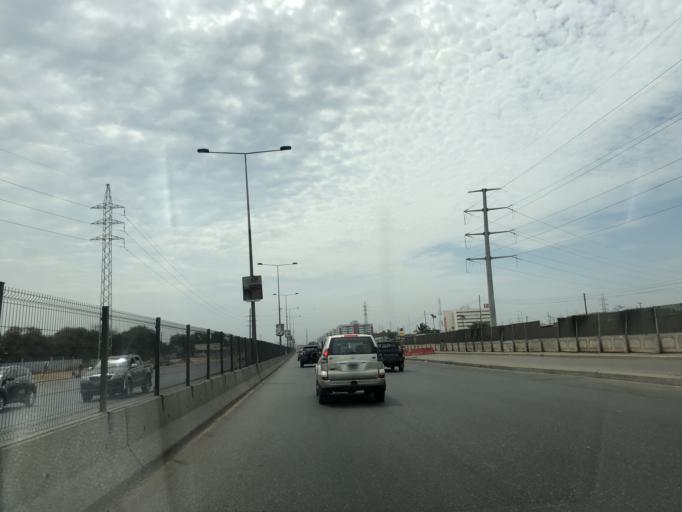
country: AO
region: Luanda
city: Luanda
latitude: -8.8570
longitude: 13.2981
